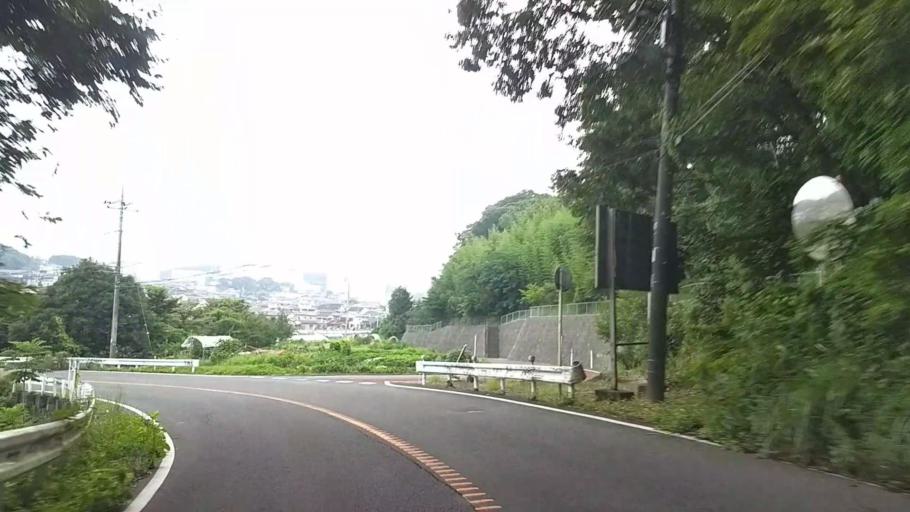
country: JP
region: Kanagawa
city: Hadano
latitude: 35.3398
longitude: 139.2365
